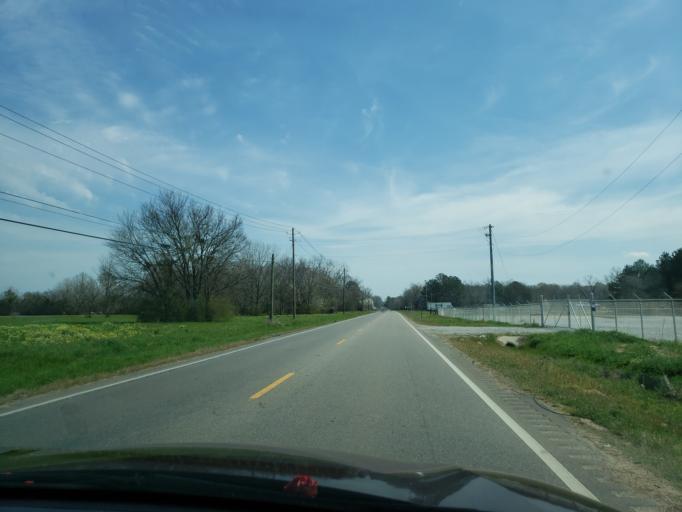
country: US
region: Alabama
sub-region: Autauga County
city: Prattville
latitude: 32.4307
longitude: -86.5108
